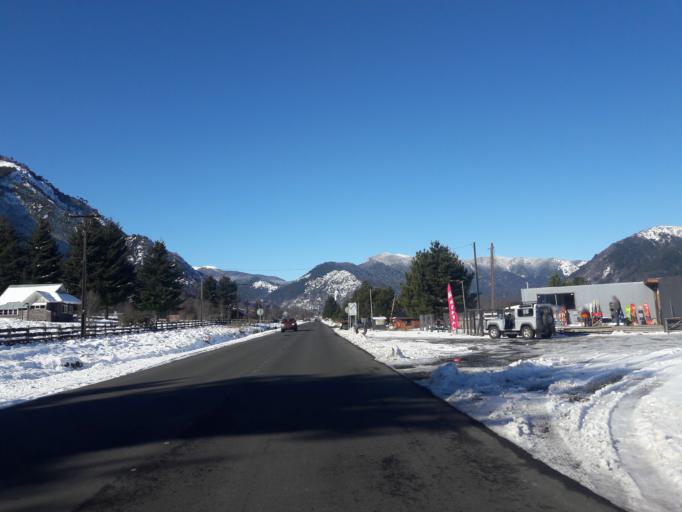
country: CL
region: Araucania
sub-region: Provincia de Cautin
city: Vilcun
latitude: -38.4714
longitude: -71.5736
